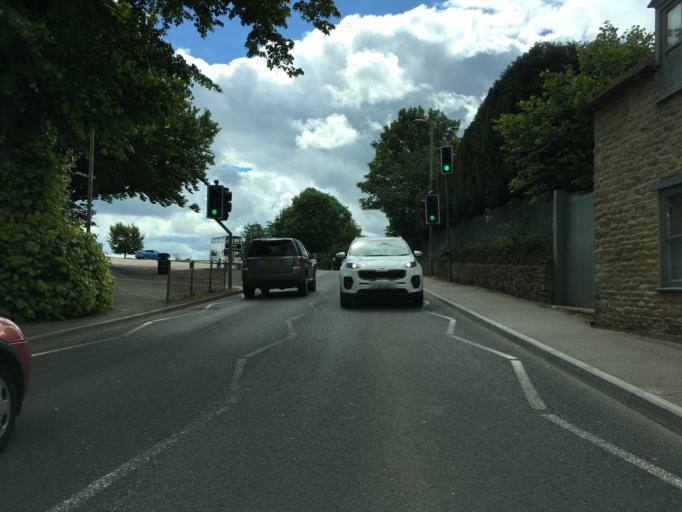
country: GB
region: England
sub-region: Oxfordshire
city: Chipping Norton
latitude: 51.9370
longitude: -1.5444
